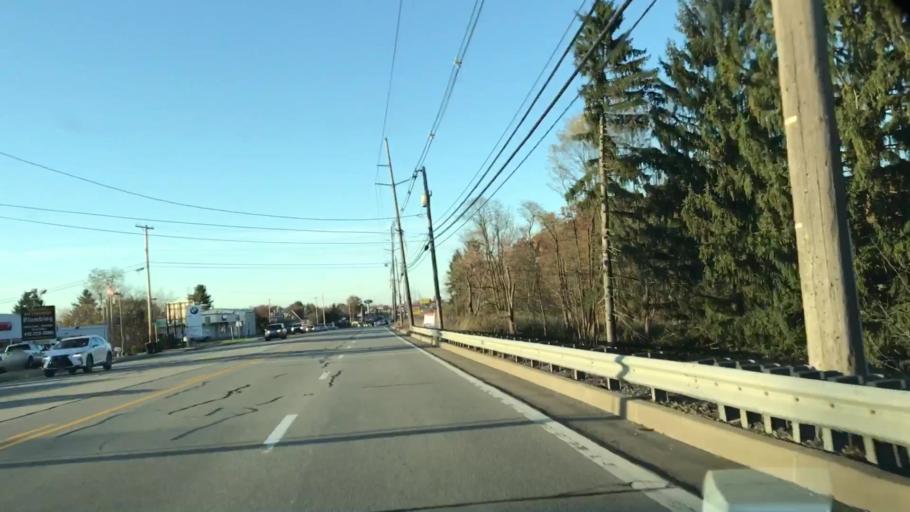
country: US
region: Pennsylvania
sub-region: Allegheny County
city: Franklin Park
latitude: 40.6008
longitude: -80.0486
